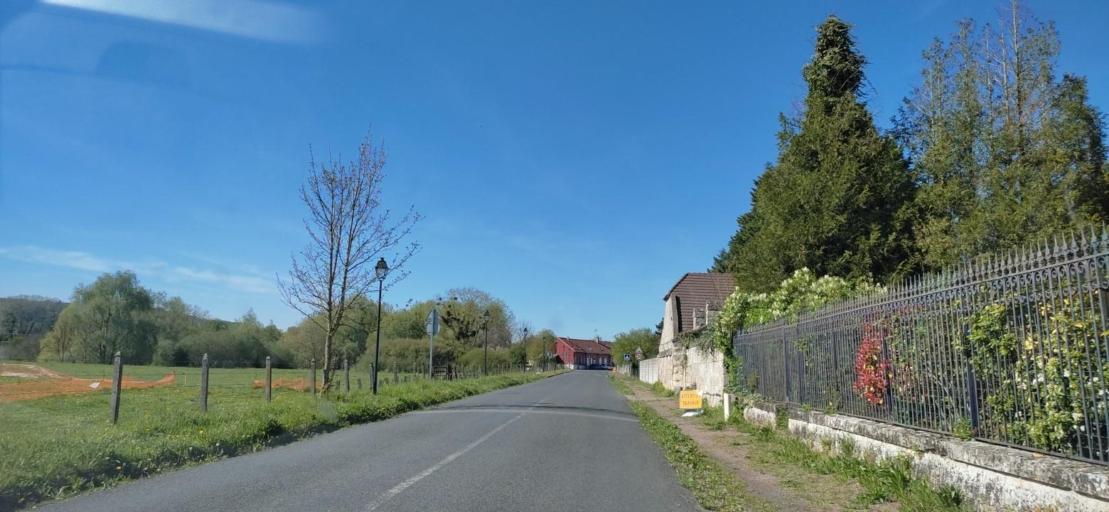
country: FR
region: Picardie
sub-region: Departement de l'Oise
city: Chiry-Ourscamp
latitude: 49.5321
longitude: 2.9721
